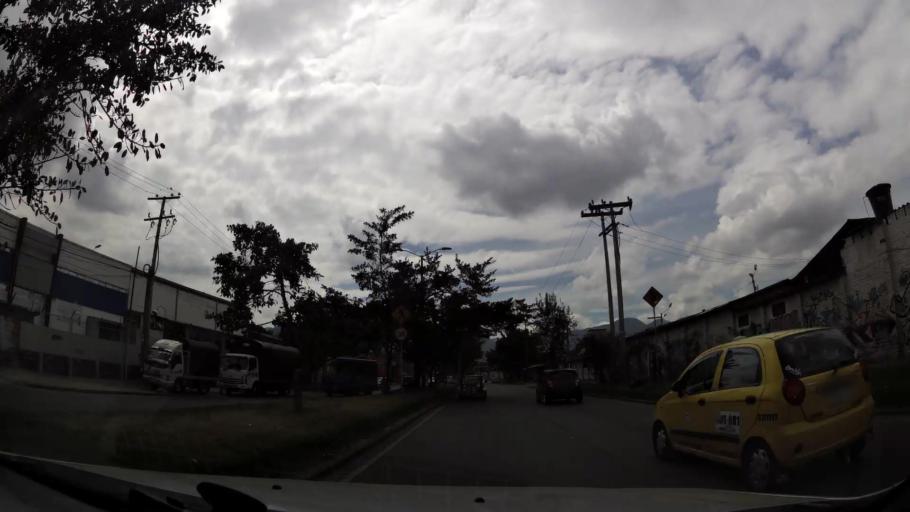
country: CO
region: Bogota D.C.
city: Bogota
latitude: 4.6072
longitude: -74.1062
